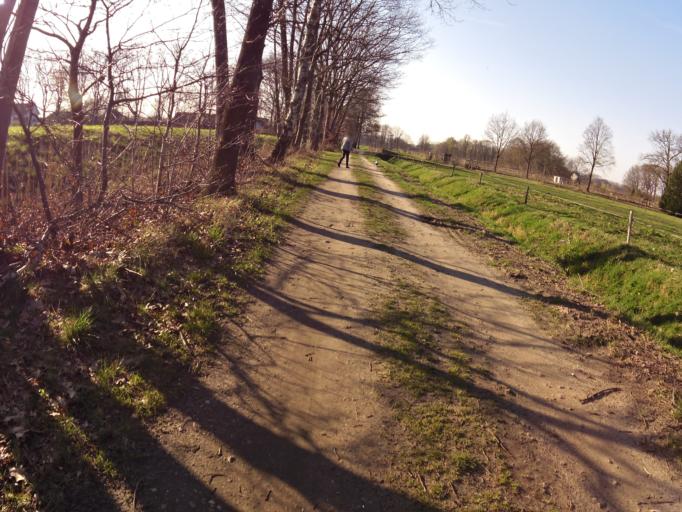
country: NL
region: North Brabant
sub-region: Gemeente Sint-Michielsgestel
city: Sint-Michielsgestel
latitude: 51.6348
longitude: 5.3265
